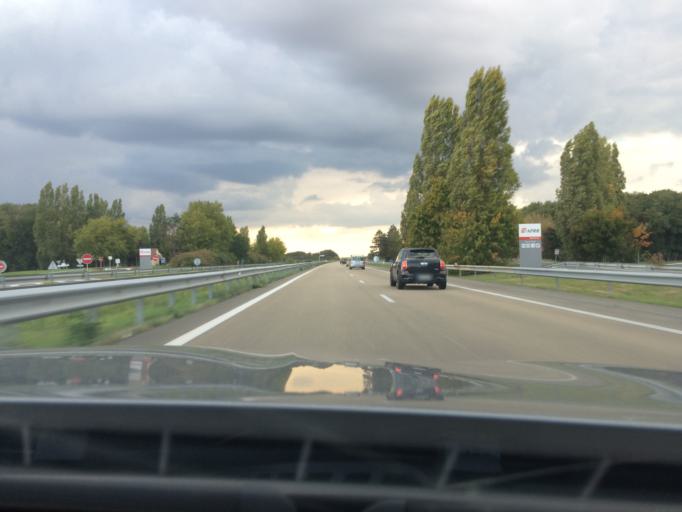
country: FR
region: Ile-de-France
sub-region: Departement de Seine-et-Marne
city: Egreville
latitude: 48.1856
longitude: 2.8289
